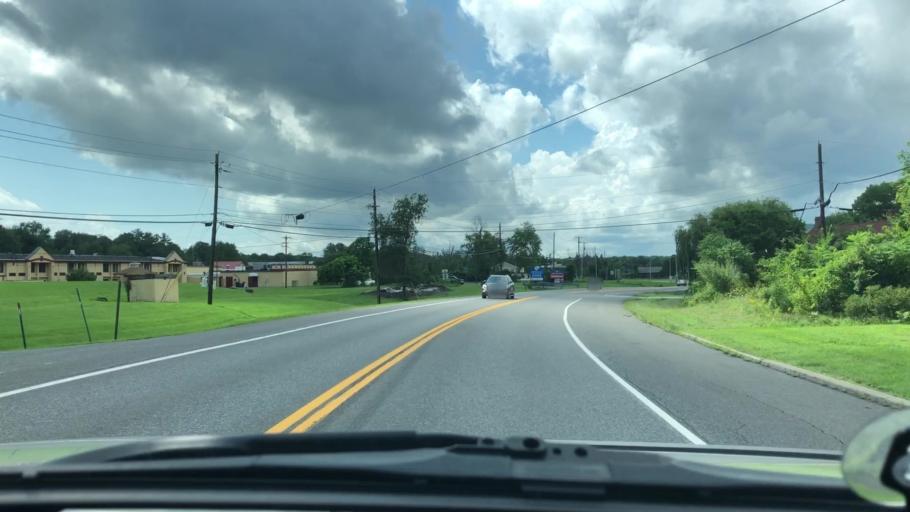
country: US
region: New York
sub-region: Ulster County
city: Saugerties
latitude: 42.0886
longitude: -73.9736
